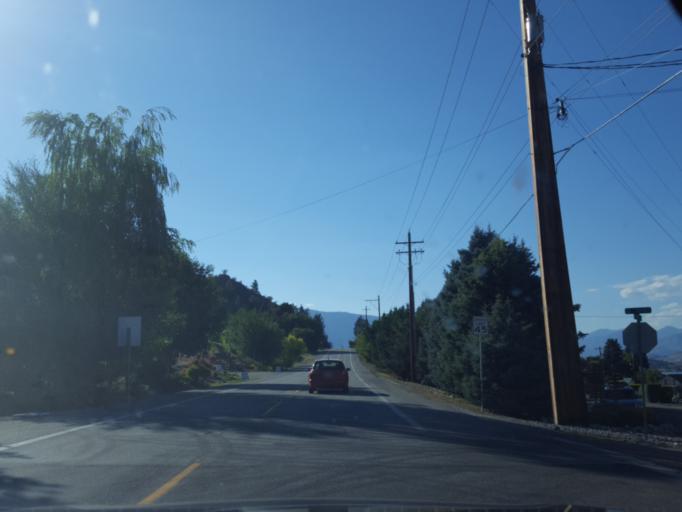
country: US
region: Washington
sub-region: Chelan County
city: Manson
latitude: 47.8477
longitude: -120.1143
